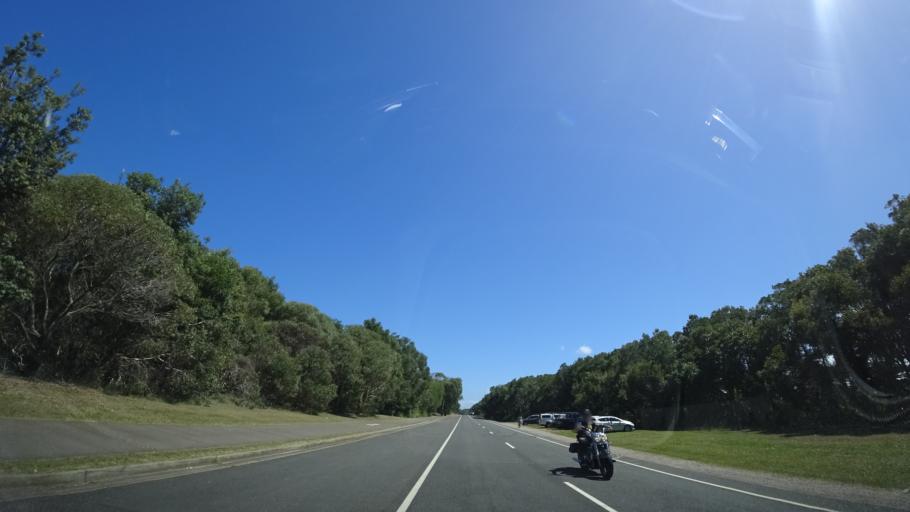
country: AU
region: Queensland
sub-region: Sunshine Coast
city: Mooloolaba
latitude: -26.6179
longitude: 153.1009
